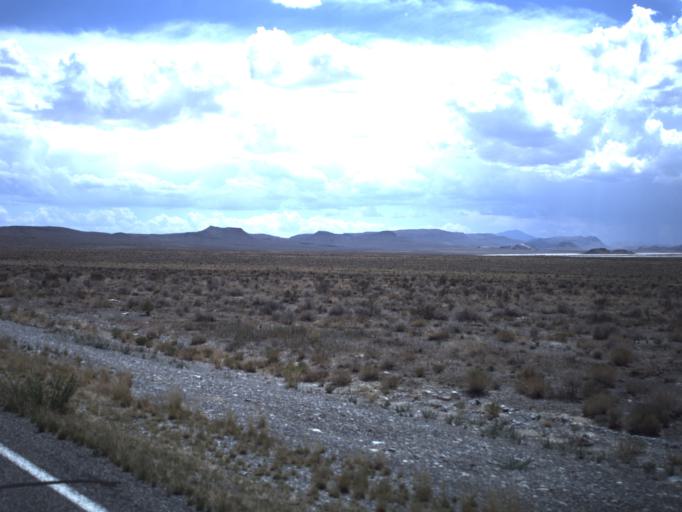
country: US
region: Utah
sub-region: Beaver County
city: Milford
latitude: 39.0278
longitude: -113.3767
